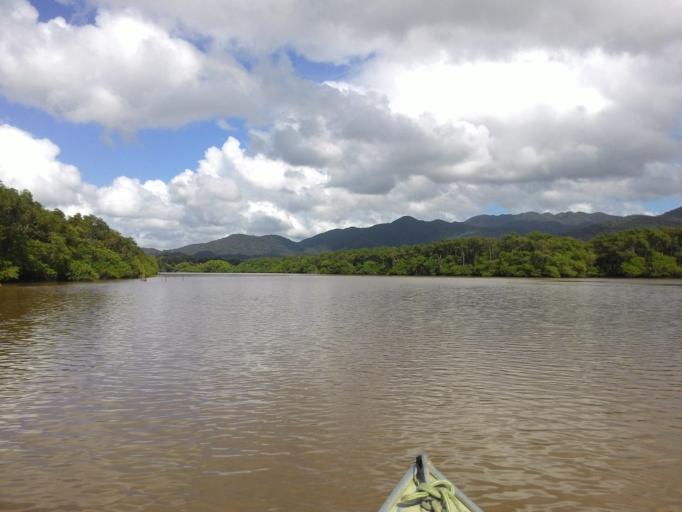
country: BR
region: Sao Paulo
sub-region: Cananeia
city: Cananeia
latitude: -24.8833
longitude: -47.8007
